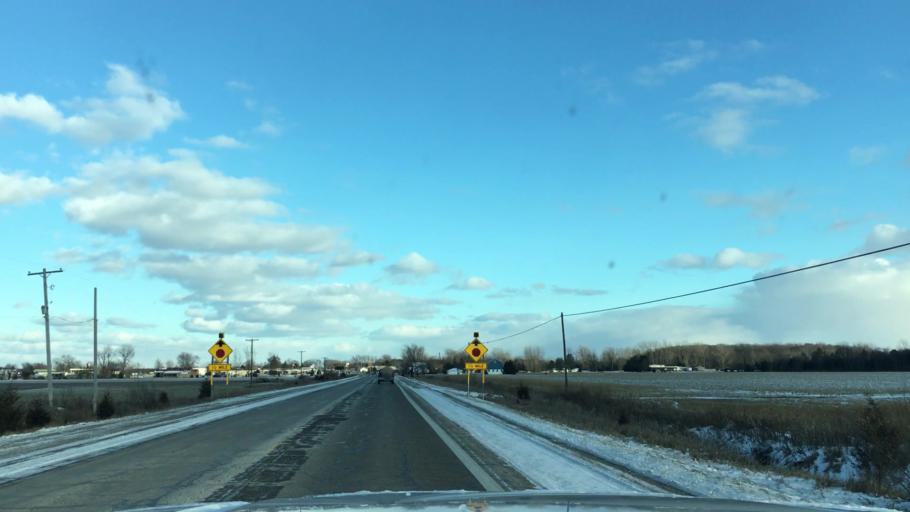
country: US
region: Michigan
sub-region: Saginaw County
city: Chesaning
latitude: 43.1866
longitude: -84.1772
